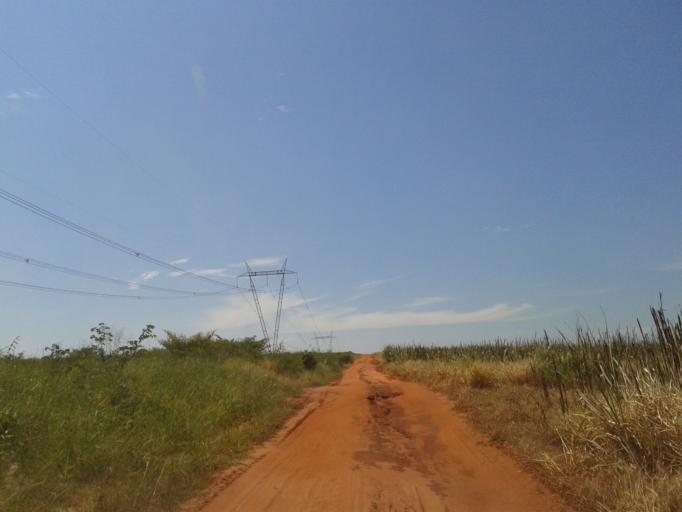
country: BR
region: Minas Gerais
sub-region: Santa Vitoria
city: Santa Vitoria
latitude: -19.0824
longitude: -50.4559
